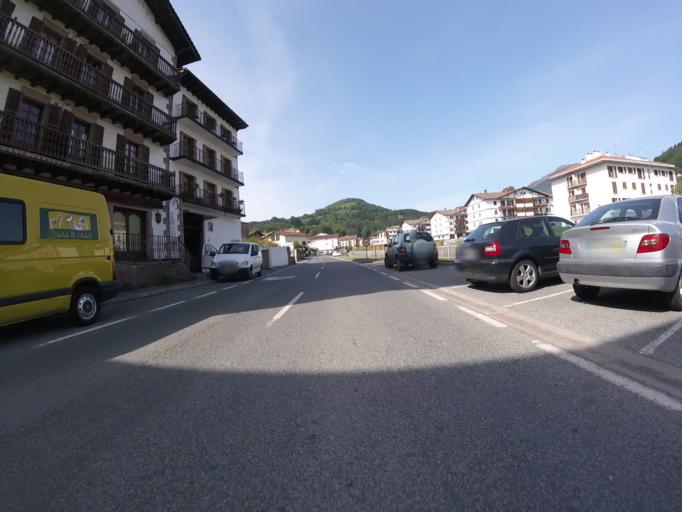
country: ES
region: Navarre
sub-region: Provincia de Navarra
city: Doneztebe
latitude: 43.1324
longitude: -1.6687
